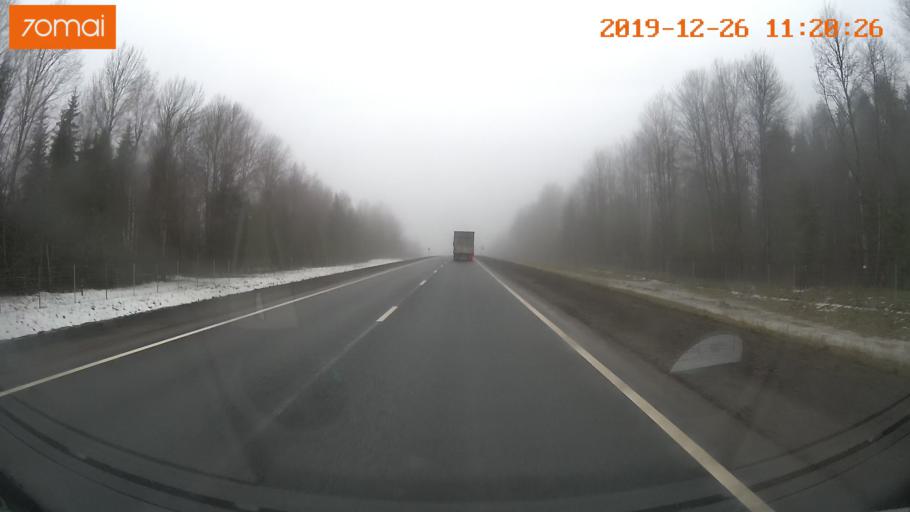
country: RU
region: Vologda
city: Chebsara
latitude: 59.1192
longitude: 38.9891
